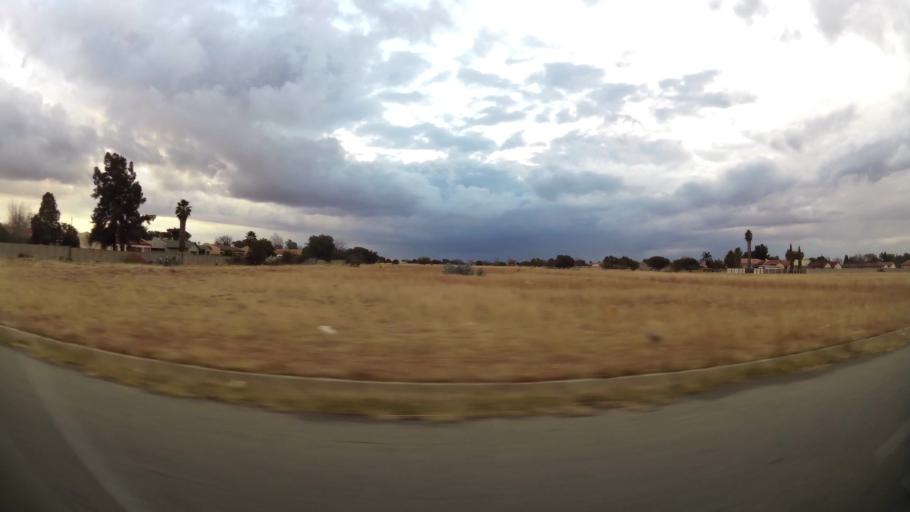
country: ZA
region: Orange Free State
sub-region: Lejweleputswa District Municipality
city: Welkom
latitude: -27.9464
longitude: 26.7349
